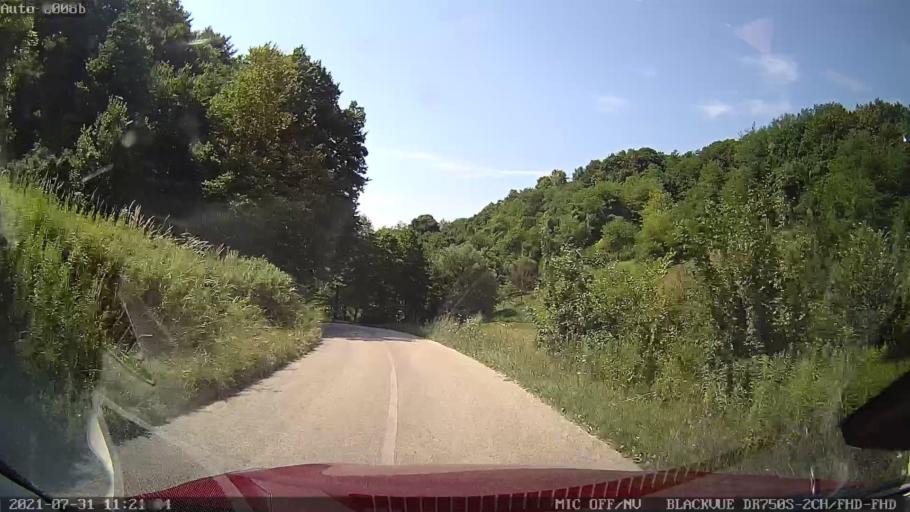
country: HR
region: Varazdinska
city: Jalzabet
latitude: 46.2296
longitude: 16.4744
